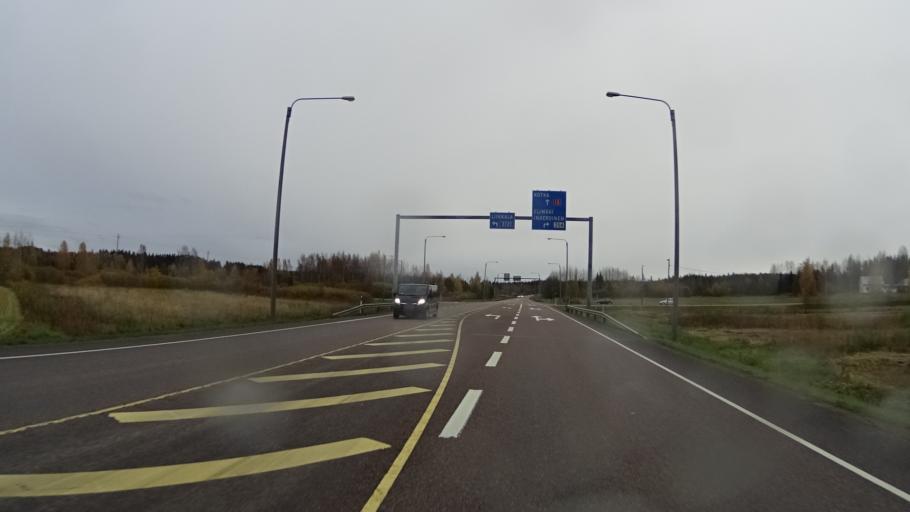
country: FI
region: Kymenlaakso
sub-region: Kouvola
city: Anjala
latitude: 60.6964
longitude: 26.8695
